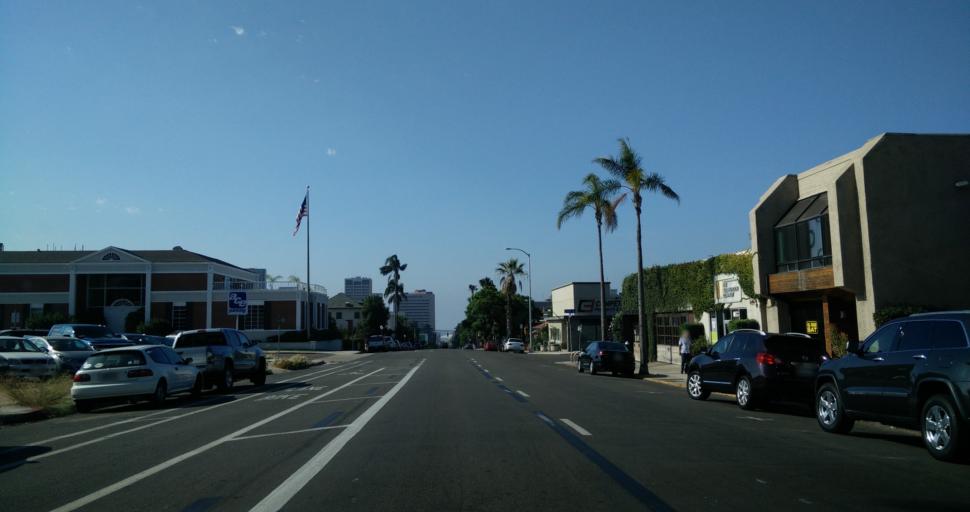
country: US
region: California
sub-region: San Diego County
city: San Diego
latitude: 32.7288
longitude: -117.1612
